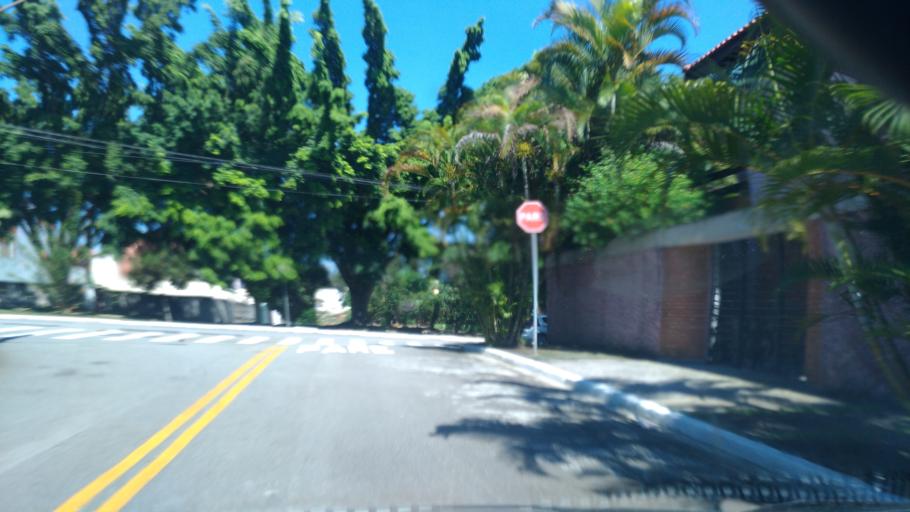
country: BR
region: Sao Paulo
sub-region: Sao Bernardo Do Campo
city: Sao Bernardo do Campo
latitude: -23.7073
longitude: -46.5802
